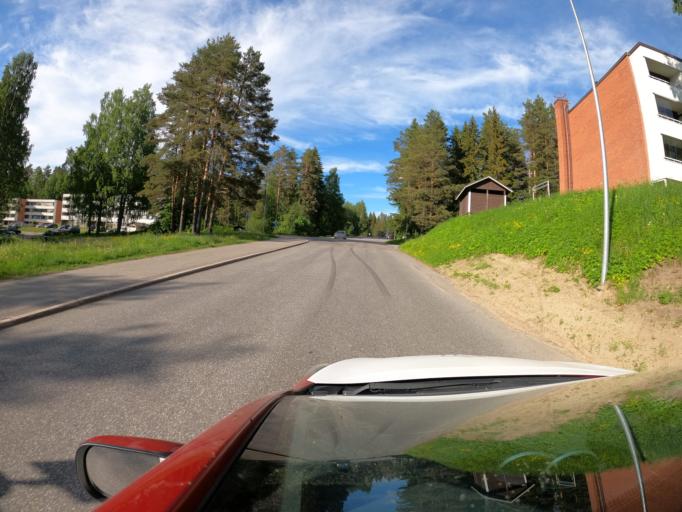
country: FI
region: Southern Savonia
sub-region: Savonlinna
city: Savonlinna
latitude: 61.8492
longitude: 28.9630
